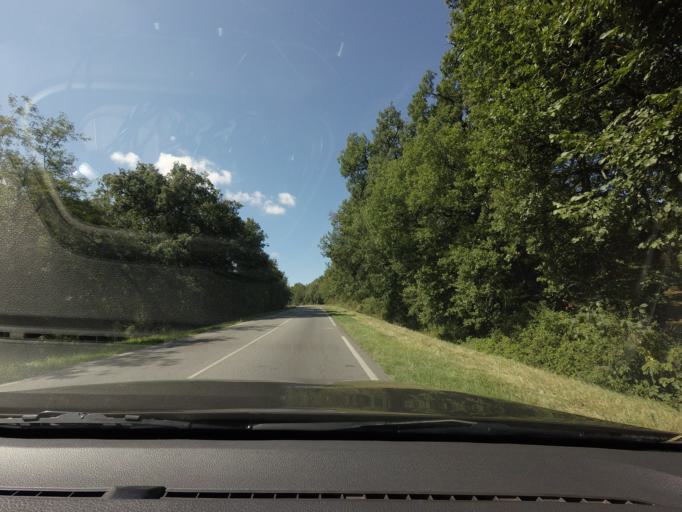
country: FR
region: Midi-Pyrenees
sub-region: Departement de la Haute-Garonne
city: Cornebarrieu
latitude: 43.6462
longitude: 1.3356
